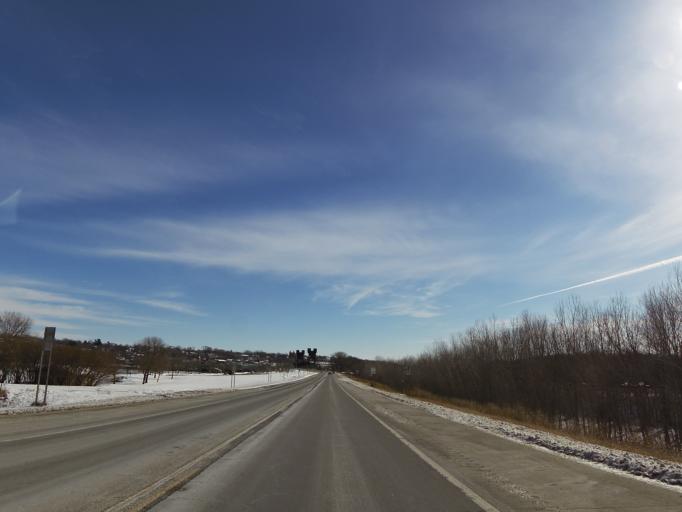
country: US
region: Wisconsin
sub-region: Pierce County
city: Prescott
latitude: 44.7496
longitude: -92.8140
